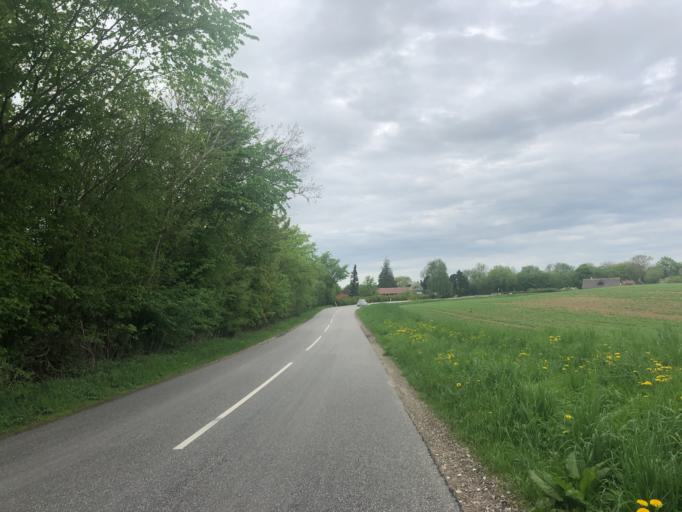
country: DK
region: Zealand
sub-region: Koge Kommune
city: Ejby
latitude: 55.4722
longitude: 12.1131
